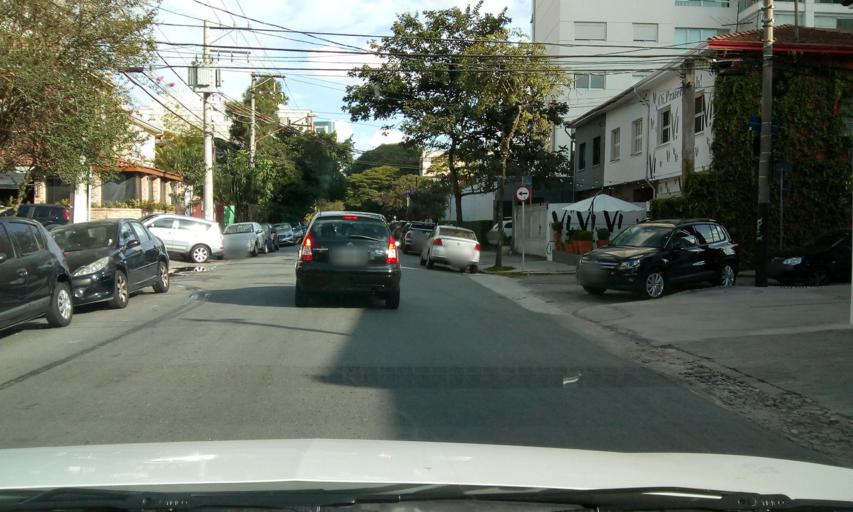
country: BR
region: Sao Paulo
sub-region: Sao Paulo
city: Sao Paulo
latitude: -23.5609
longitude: -46.6991
